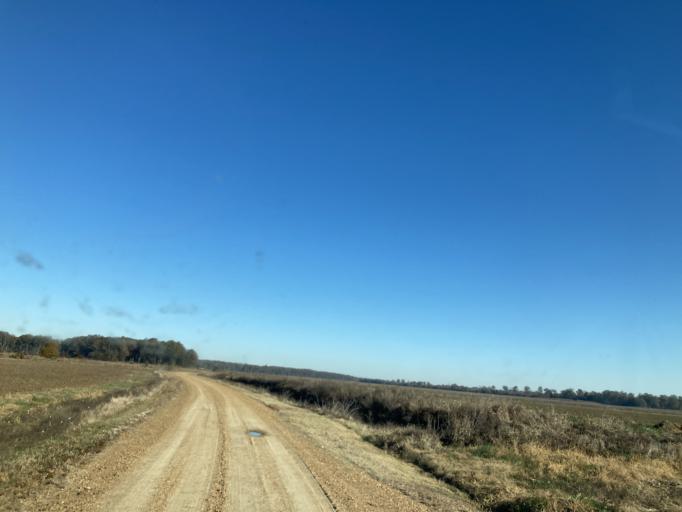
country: US
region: Mississippi
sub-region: Sharkey County
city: Rolling Fork
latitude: 32.8993
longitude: -90.6643
